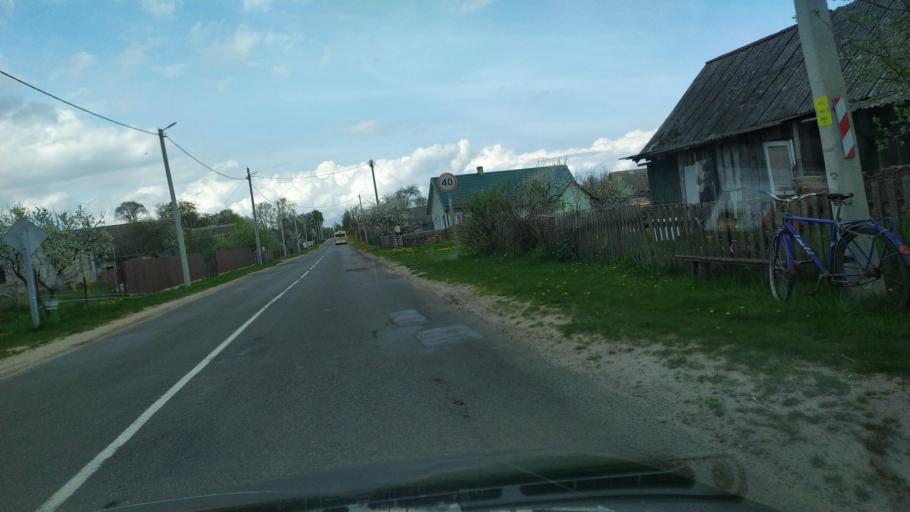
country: BY
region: Brest
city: Pruzhany
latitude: 52.5809
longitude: 24.4120
